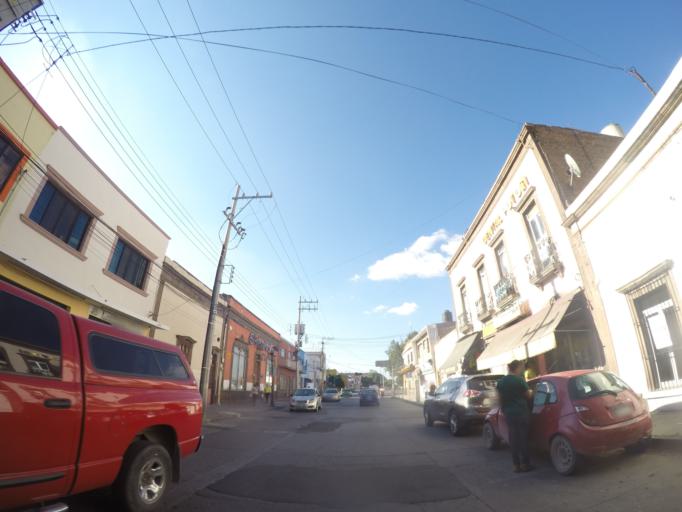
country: MX
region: San Luis Potosi
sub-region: San Luis Potosi
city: San Luis Potosi
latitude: 22.1556
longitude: -100.9793
